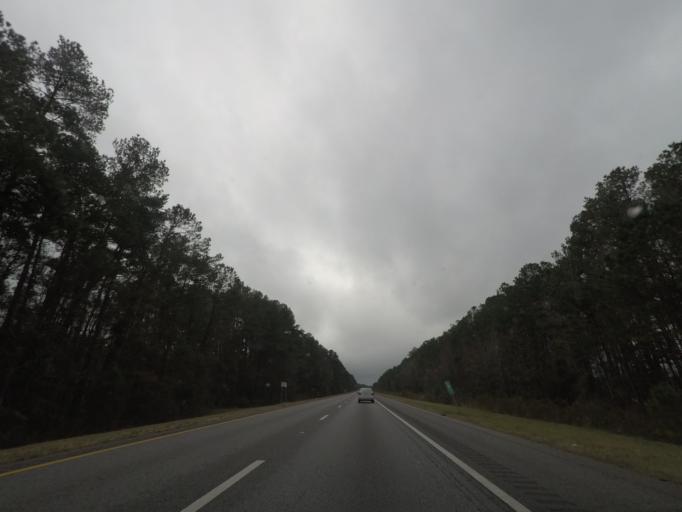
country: US
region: South Carolina
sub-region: Orangeburg County
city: Holly Hill
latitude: 33.3353
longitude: -80.5381
